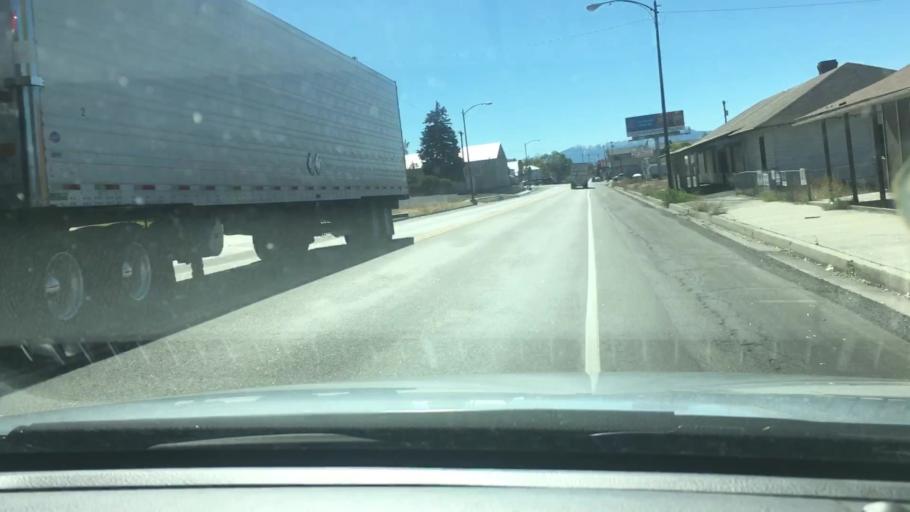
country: US
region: Nevada
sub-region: White Pine County
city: McGill
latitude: 39.4070
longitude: -114.7779
